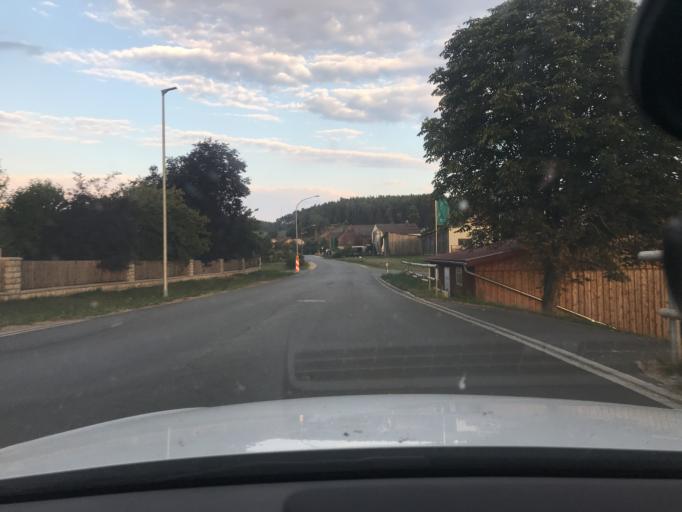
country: DE
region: Bavaria
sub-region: Upper Palatinate
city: Auerbach
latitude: 49.7224
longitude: 11.6157
